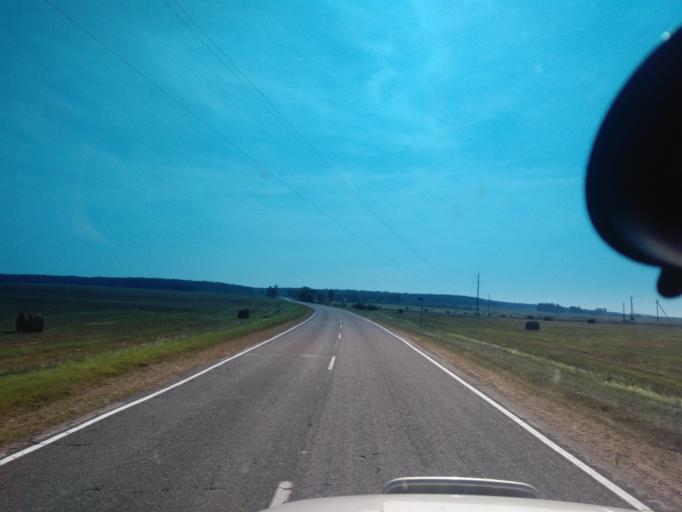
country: BY
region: Minsk
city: Uzda
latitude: 53.3952
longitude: 27.2331
